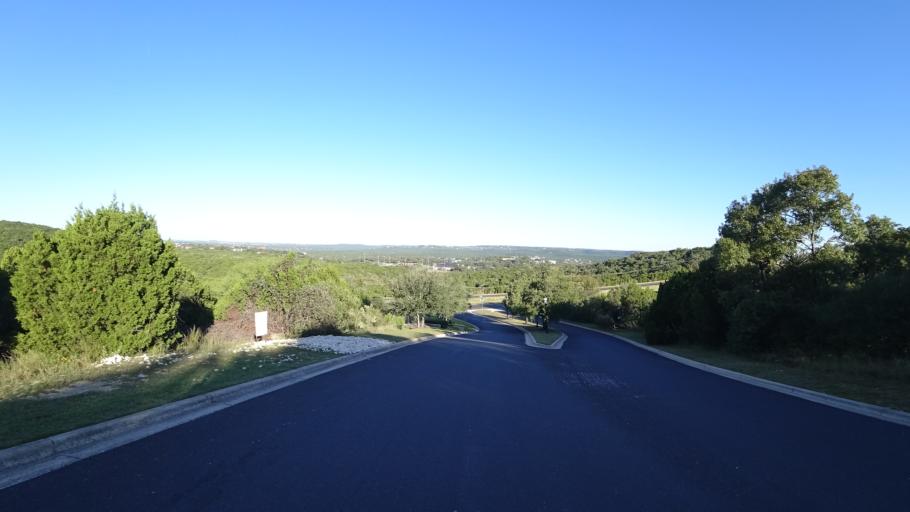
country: US
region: Texas
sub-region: Travis County
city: West Lake Hills
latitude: 30.3219
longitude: -97.8136
